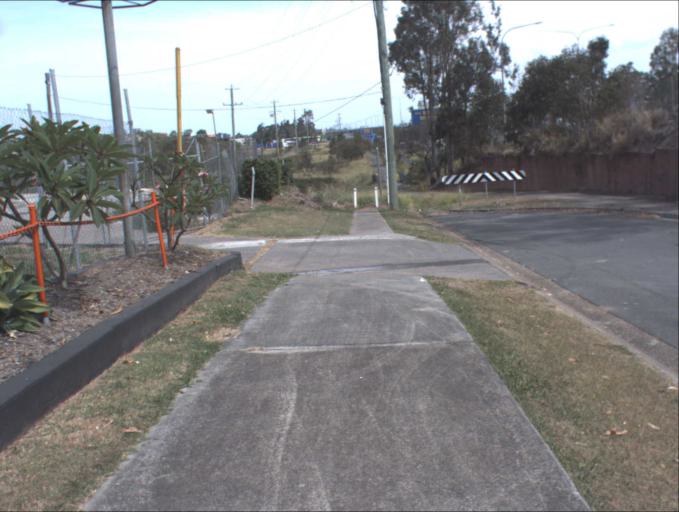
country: AU
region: Queensland
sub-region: Logan
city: Beenleigh
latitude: -27.6786
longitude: 153.1863
